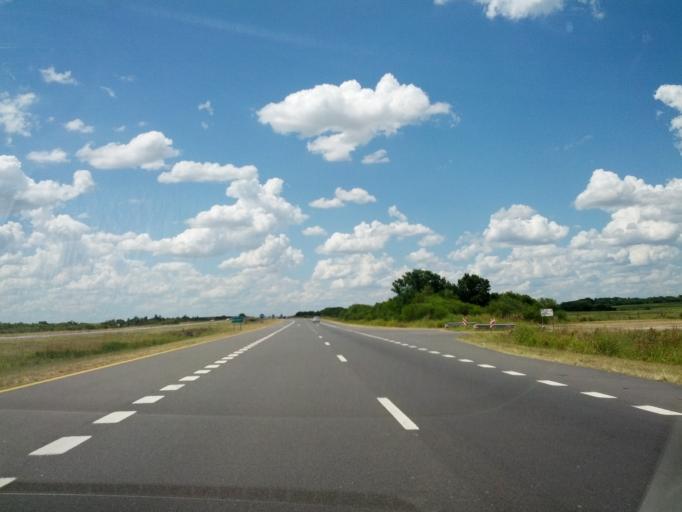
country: AR
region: Entre Rios
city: Colonia Elia
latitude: -32.7460
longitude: -58.4791
